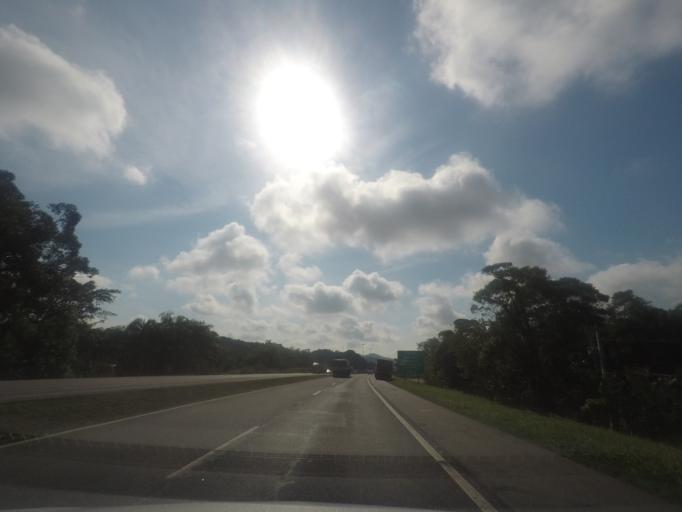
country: BR
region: Parana
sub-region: Antonina
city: Antonina
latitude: -25.5535
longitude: -48.8013
